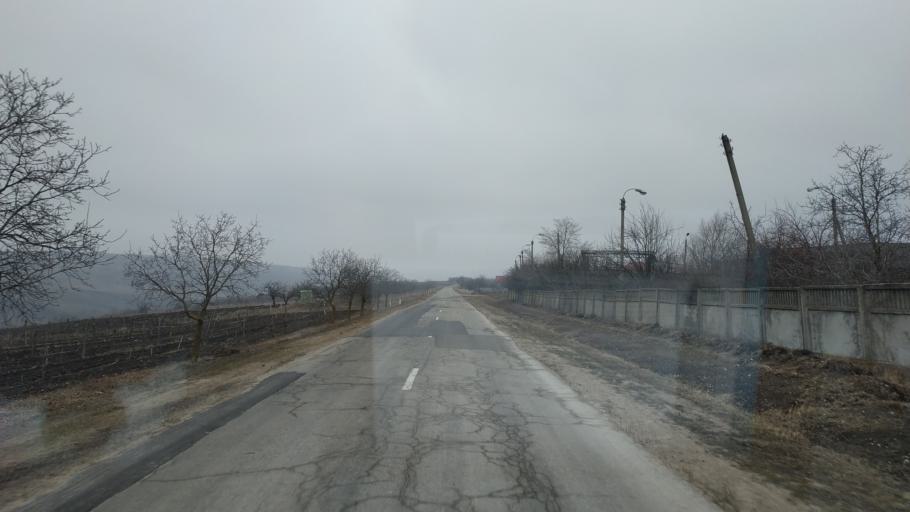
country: MD
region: Stinga Nistrului
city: Bucovat
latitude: 47.0262
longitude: 28.4239
